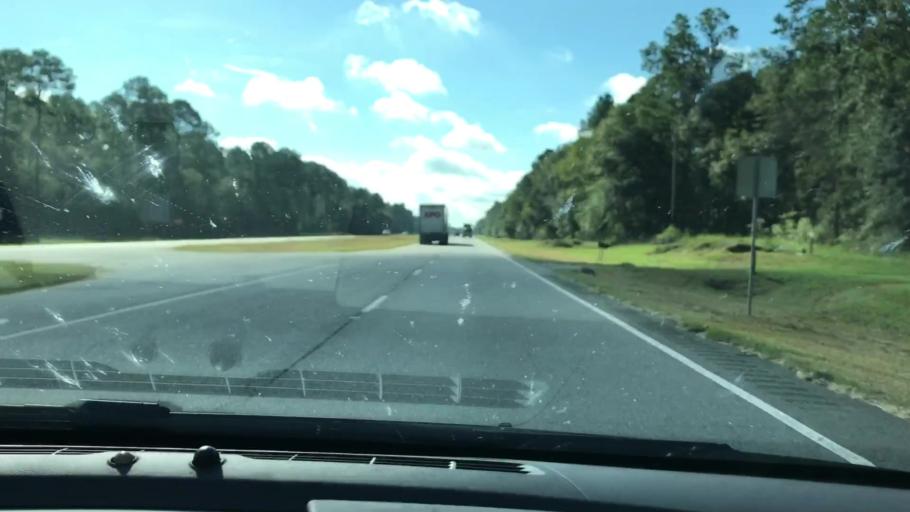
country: US
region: Georgia
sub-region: Dougherty County
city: Albany
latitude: 31.5665
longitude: -84.0185
